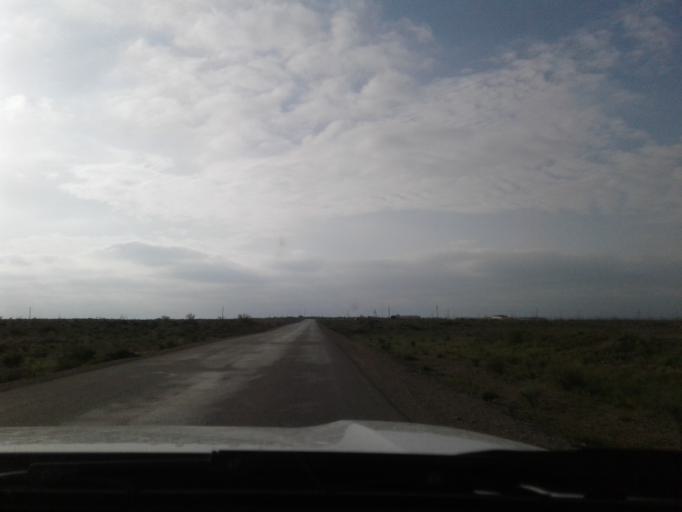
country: TM
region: Lebap
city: Sayat
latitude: 38.6332
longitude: 64.5874
